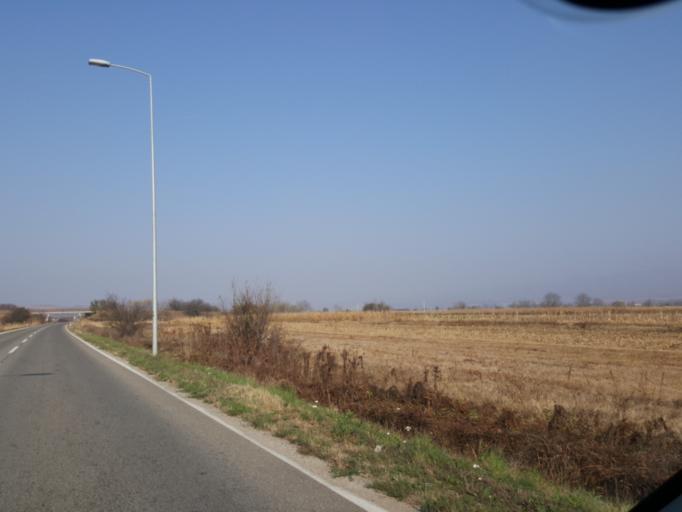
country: RS
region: Central Serbia
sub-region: Jablanicki Okrug
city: Leskovac
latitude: 43.0306
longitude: 21.9428
